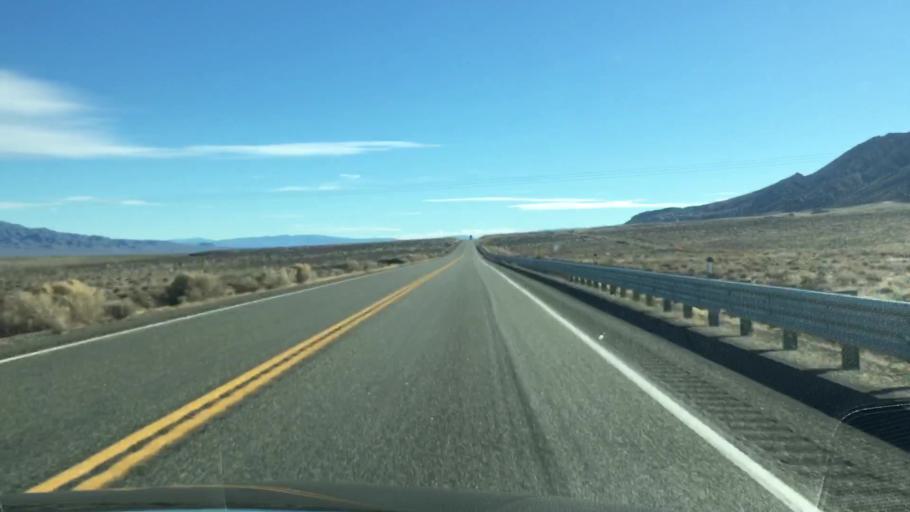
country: US
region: Nevada
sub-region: Mineral County
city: Hawthorne
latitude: 38.8125
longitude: -118.7656
